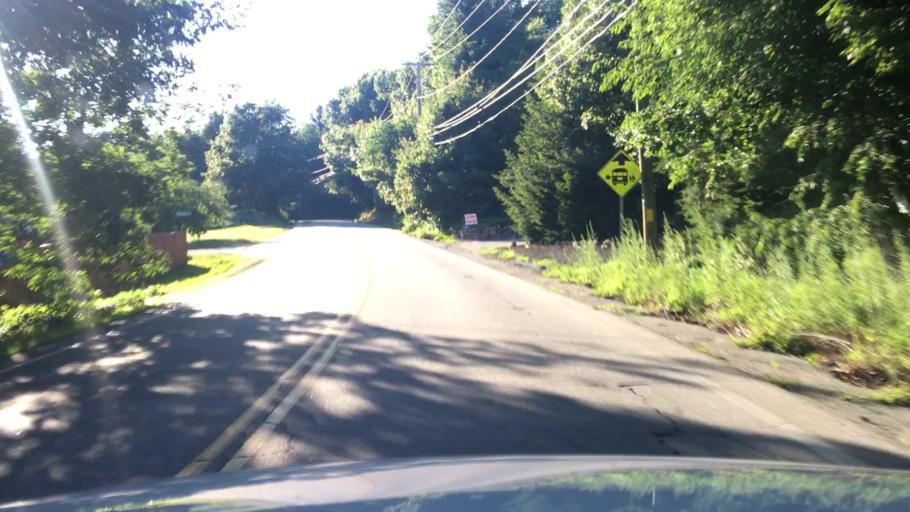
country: US
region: New Hampshire
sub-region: Rockingham County
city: Sandown
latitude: 42.9164
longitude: -71.1655
